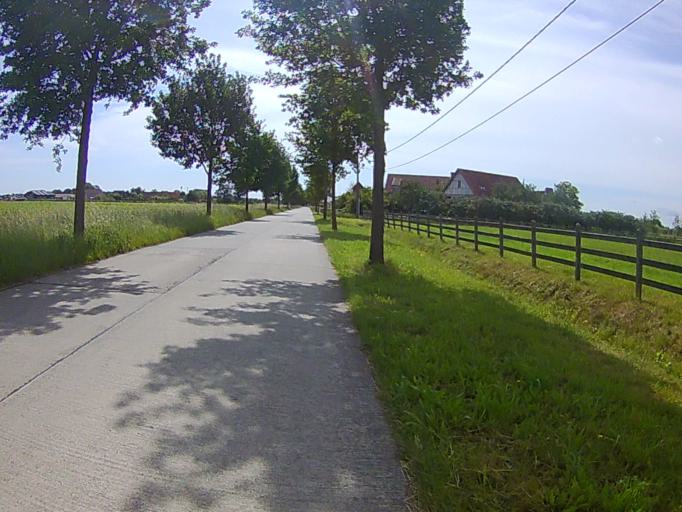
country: BE
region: Flanders
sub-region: Provincie Antwerpen
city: Lier
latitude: 51.0915
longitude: 4.5920
